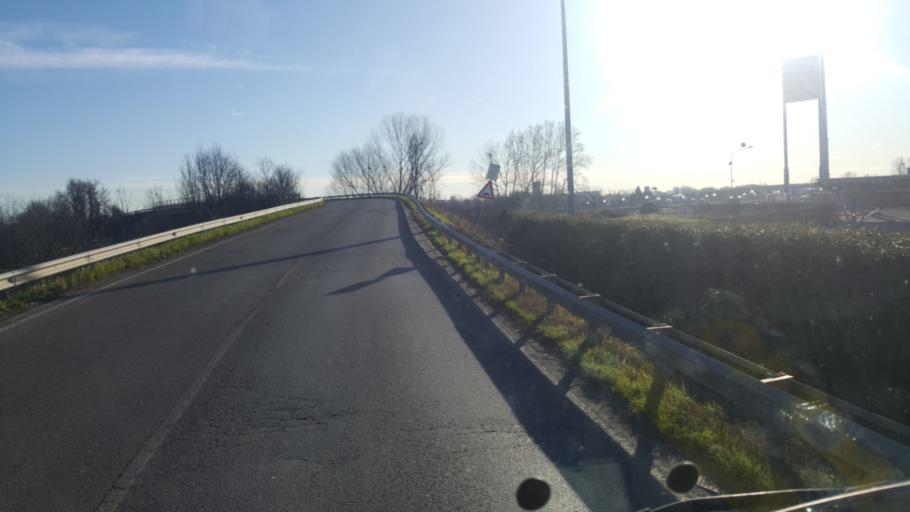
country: IT
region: Emilia-Romagna
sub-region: Provincia di Modena
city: Campogalliano
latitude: 44.6570
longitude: 10.8590
